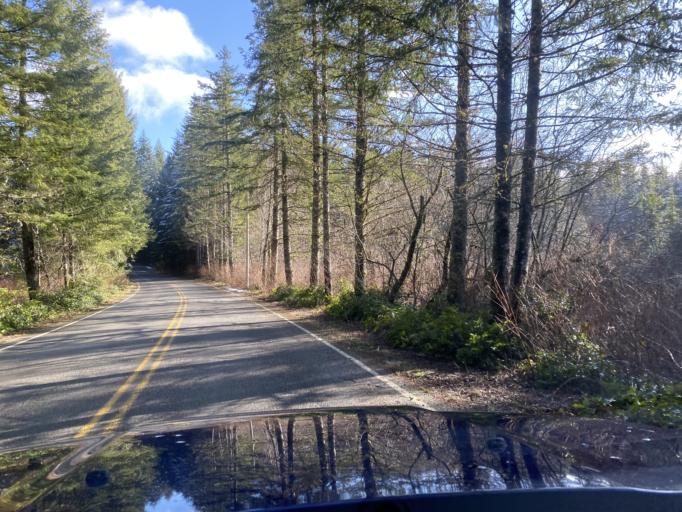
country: US
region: Washington
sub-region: King County
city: Fall City
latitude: 47.5118
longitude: -121.8915
